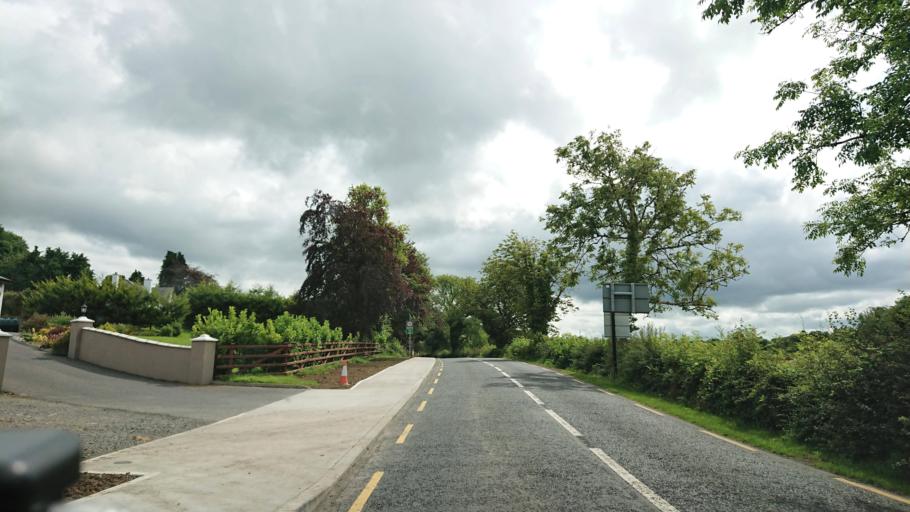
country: IE
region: Connaught
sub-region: County Leitrim
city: Carrick-on-Shannon
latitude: 54.0528
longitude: -8.1481
